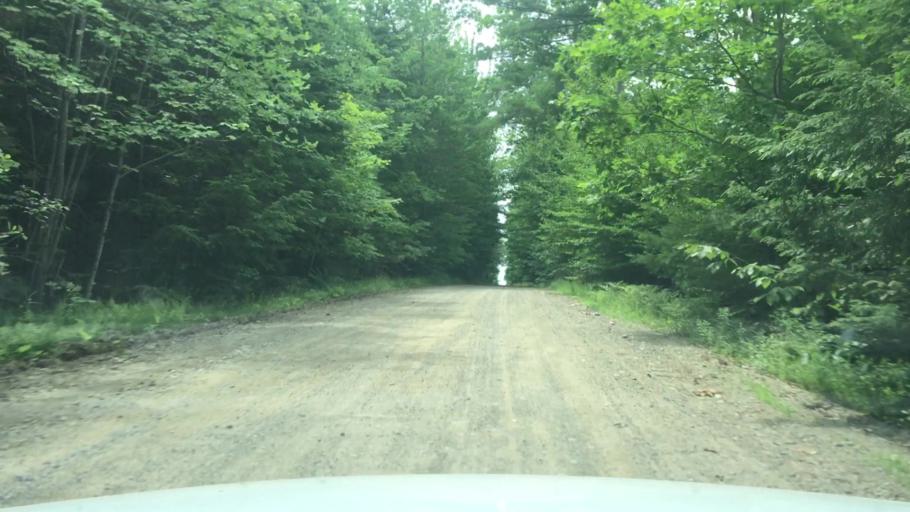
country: US
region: Maine
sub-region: Waldo County
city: Searsmont
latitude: 44.4085
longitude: -69.2707
